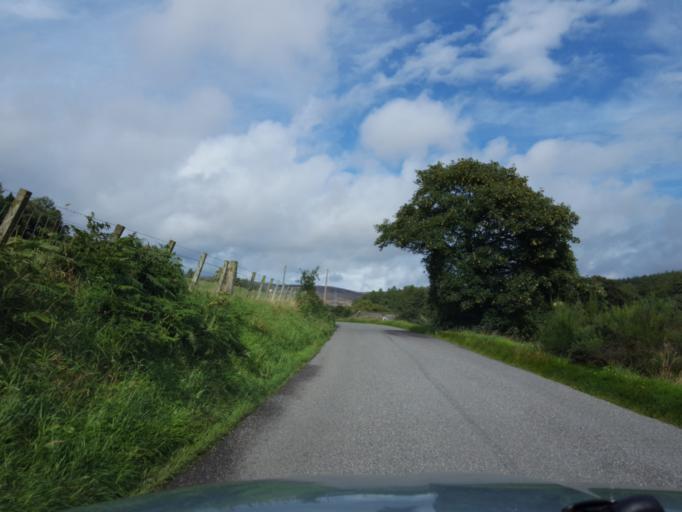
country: GB
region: Scotland
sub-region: Aberdeenshire
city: Laurencekirk
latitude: 56.8748
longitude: -2.5486
